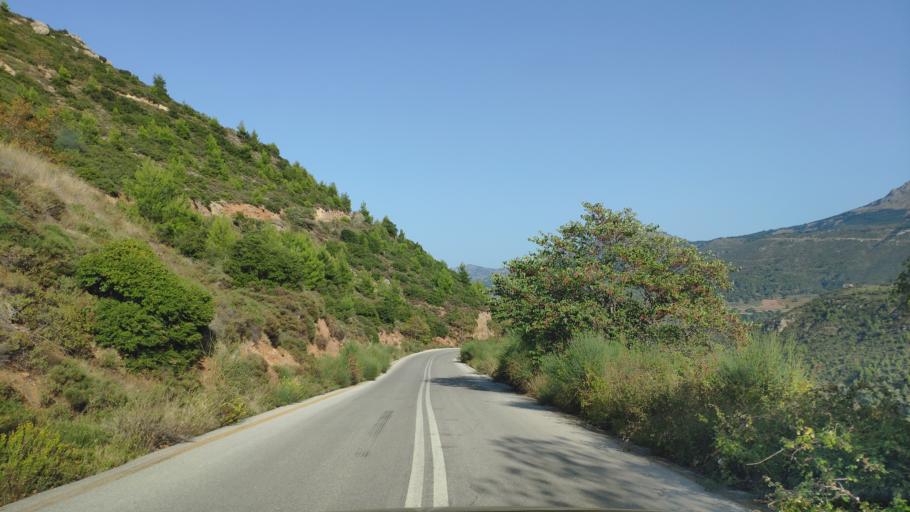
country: GR
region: West Greece
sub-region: Nomos Achaias
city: Aiyira
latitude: 38.0682
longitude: 22.3830
